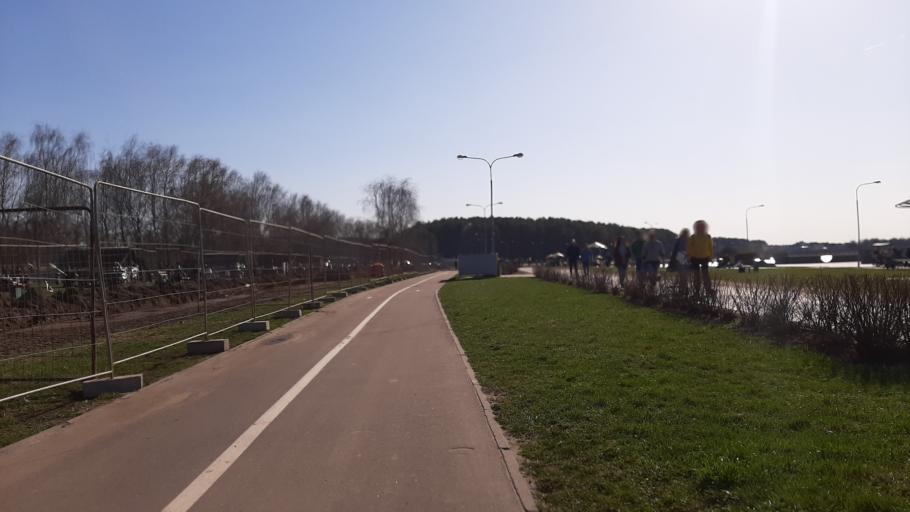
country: BY
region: Minsk
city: Bal'shavik
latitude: 53.9548
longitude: 27.5854
